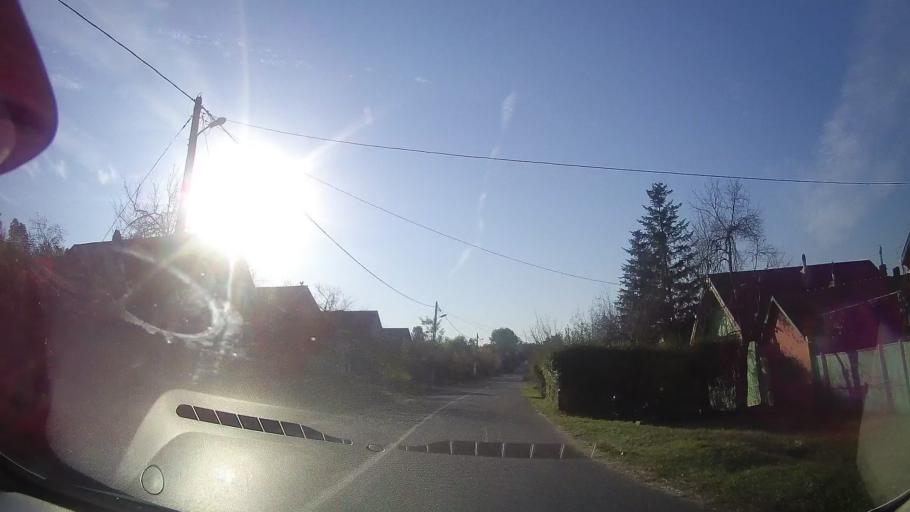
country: RO
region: Timis
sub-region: Comuna Bogda
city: Bogda
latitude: 45.9640
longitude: 21.6123
